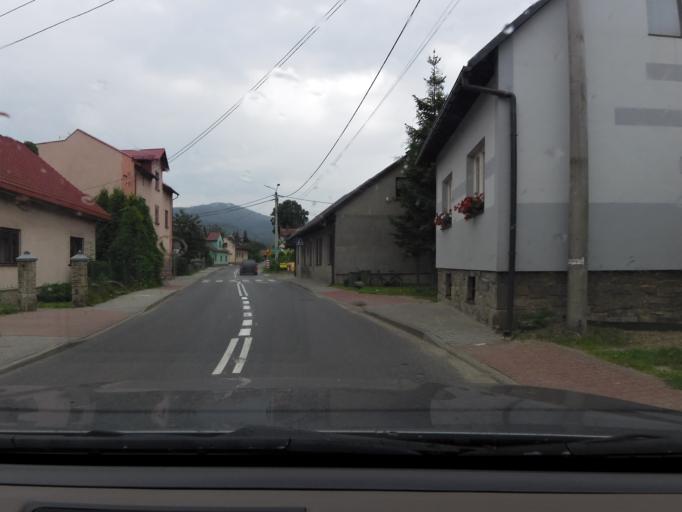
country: PL
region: Silesian Voivodeship
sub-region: Powiat zywiecki
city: Milowka
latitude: 49.5546
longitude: 19.0894
